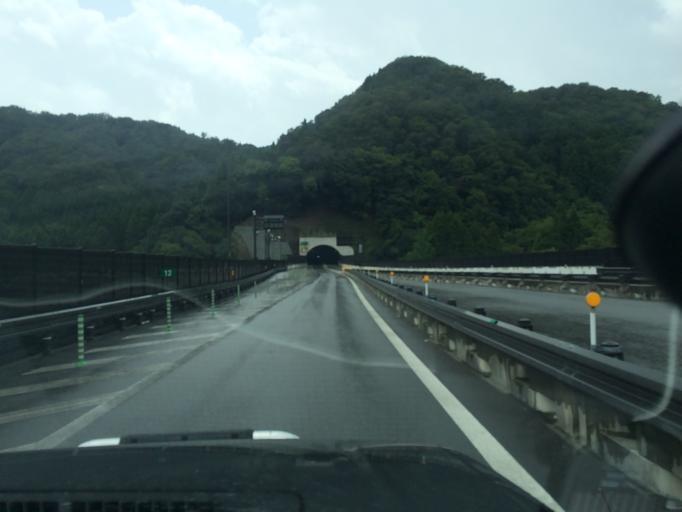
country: JP
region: Hyogo
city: Toyooka
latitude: 35.4654
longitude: 134.7636
